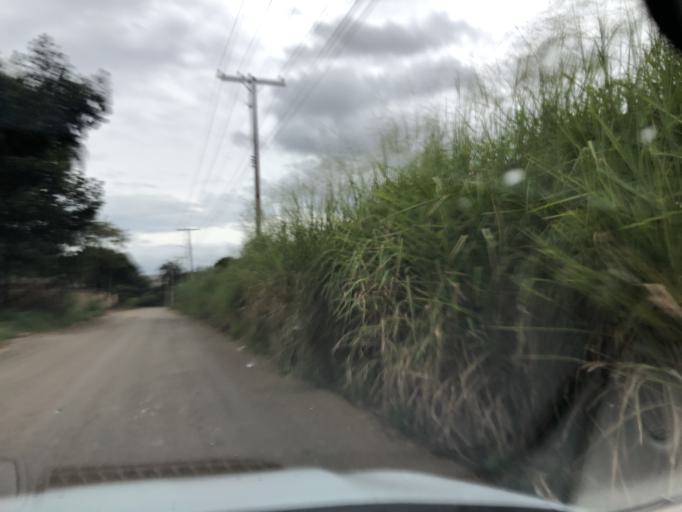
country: BR
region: Goias
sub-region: Luziania
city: Luziania
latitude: -16.1588
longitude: -47.9477
